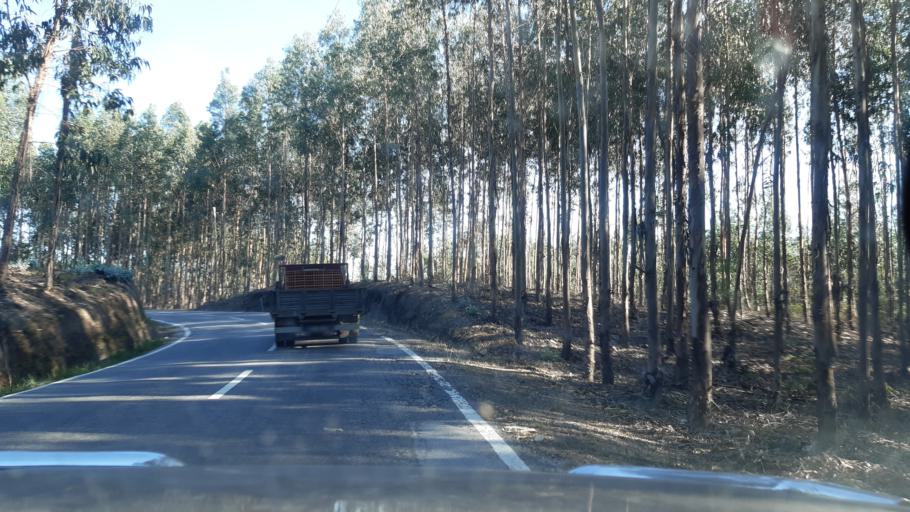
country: PT
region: Aveiro
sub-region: Agueda
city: Aguada de Cima
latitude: 40.5647
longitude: -8.3777
